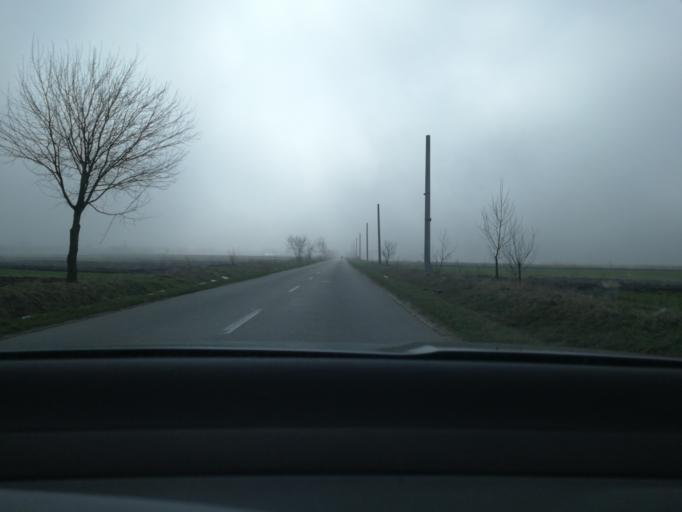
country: RO
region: Prahova
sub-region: Comuna Magureni
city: Lunca Prahovei
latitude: 45.0304
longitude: 25.7684
